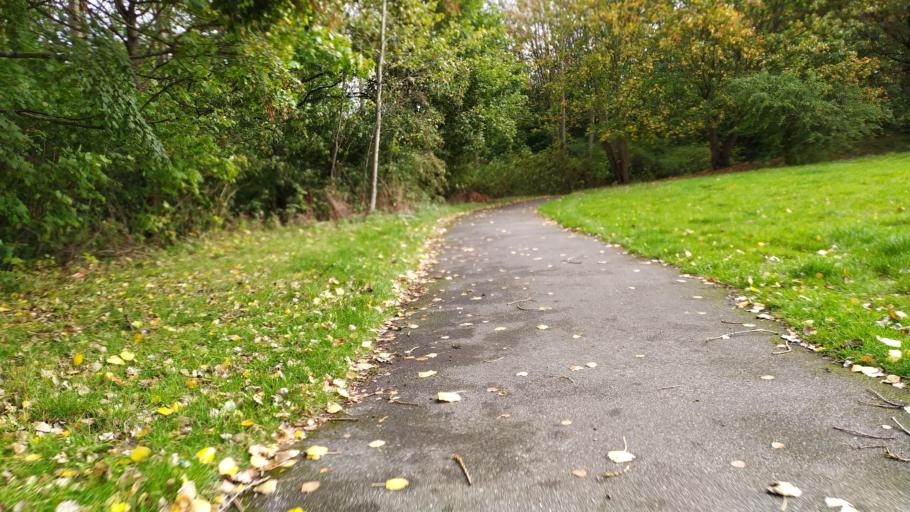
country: GB
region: England
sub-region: City and Borough of Leeds
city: Chapel Allerton
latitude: 53.8131
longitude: -1.5443
